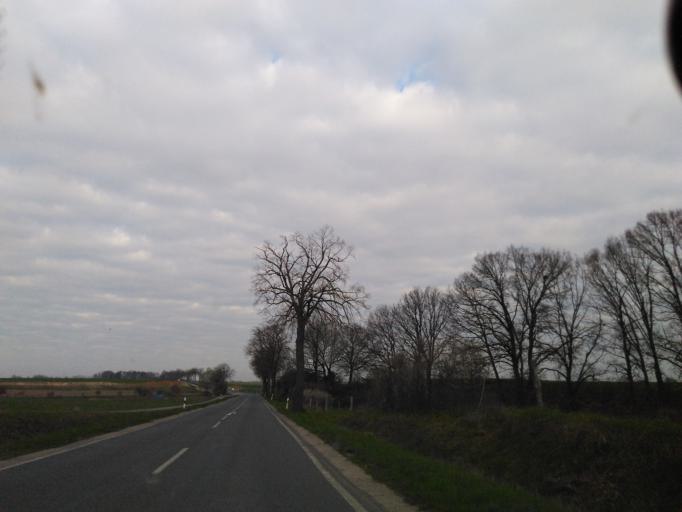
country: DE
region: Brandenburg
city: Protzel
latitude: 52.5670
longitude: 13.9652
